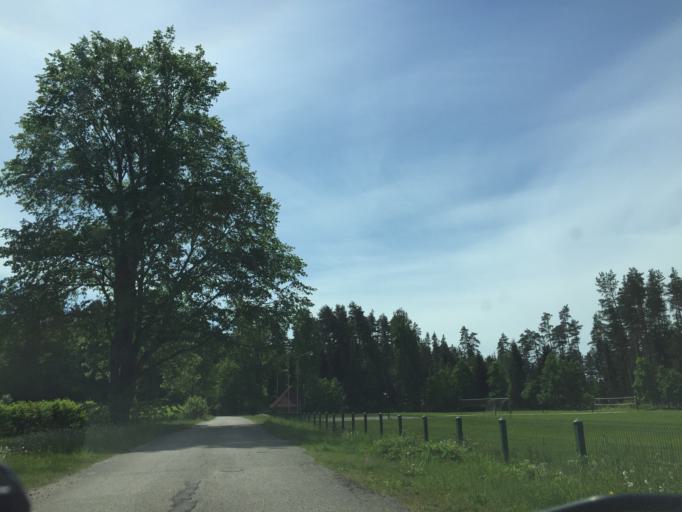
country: LV
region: Koceni
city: Koceni
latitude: 57.4607
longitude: 25.2699
